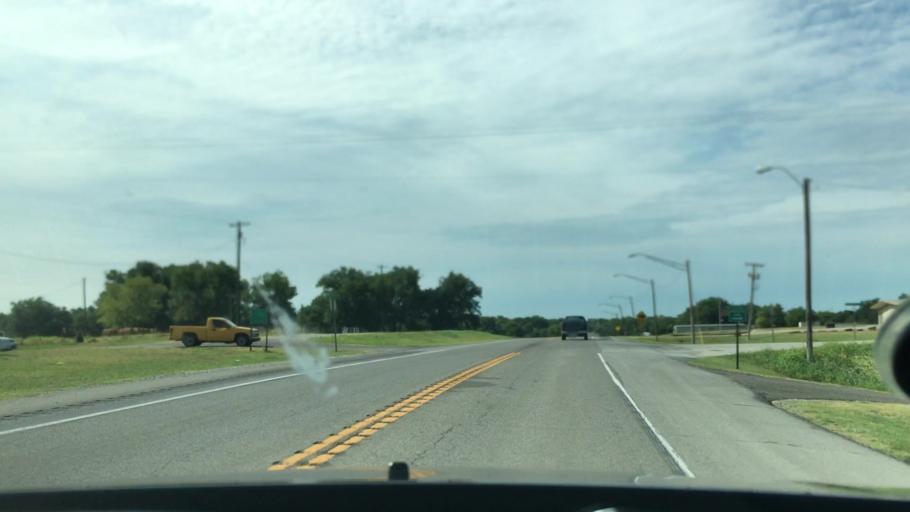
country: US
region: Oklahoma
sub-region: Murray County
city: Sulphur
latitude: 34.5213
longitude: -96.9689
